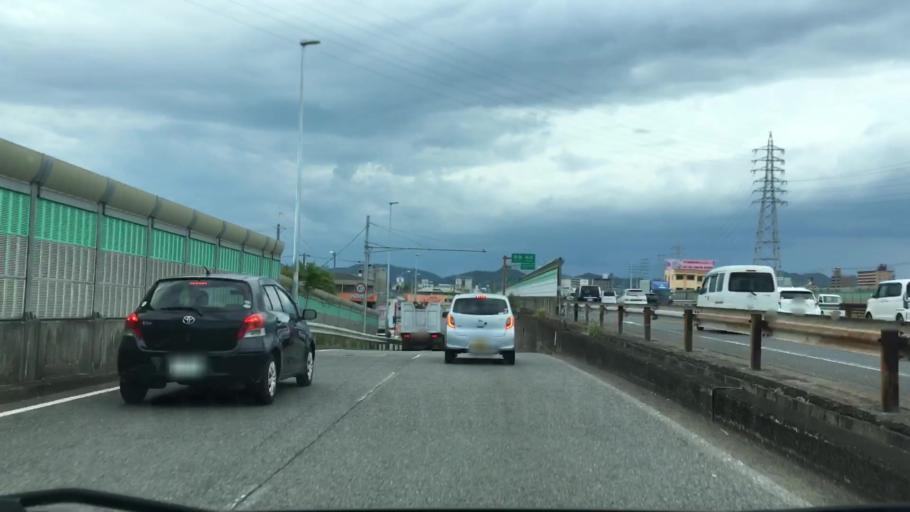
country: JP
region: Hyogo
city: Himeji
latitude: 34.8084
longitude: 134.6928
